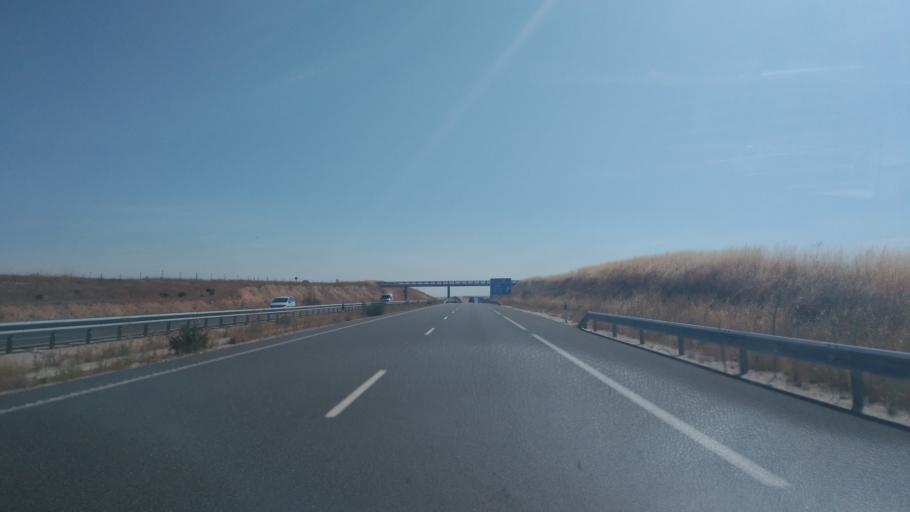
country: ES
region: Castille and Leon
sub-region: Provincia de Salamanca
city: Cordovilla
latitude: 40.9290
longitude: -5.4012
